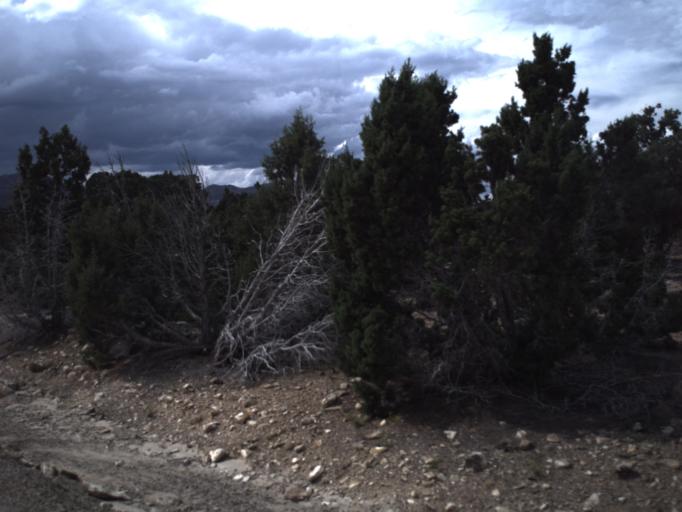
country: US
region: Utah
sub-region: Carbon County
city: Price
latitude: 39.4838
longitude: -110.9184
